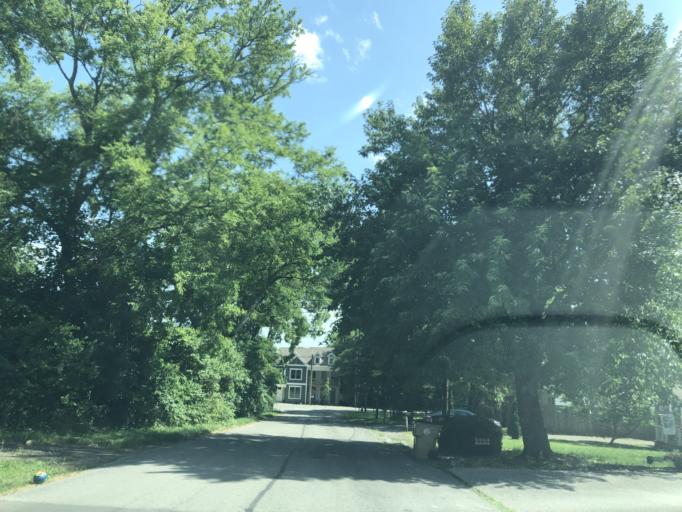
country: US
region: Tennessee
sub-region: Davidson County
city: Oak Hill
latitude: 36.0991
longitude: -86.7466
